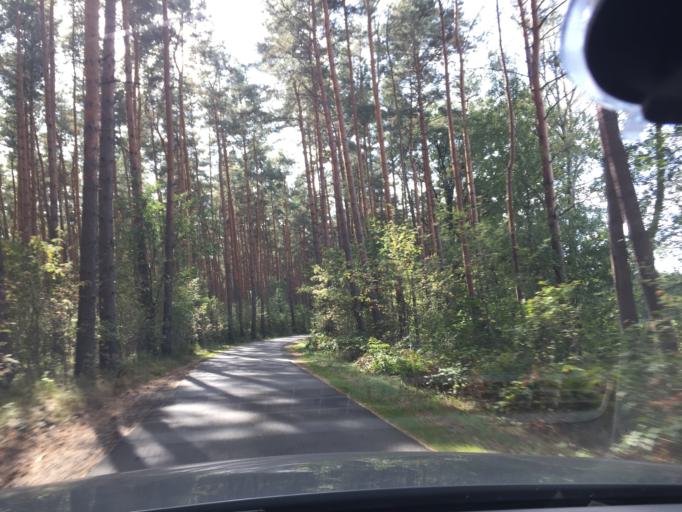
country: DE
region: Brandenburg
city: Spreenhagen
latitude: 52.3762
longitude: 13.8975
